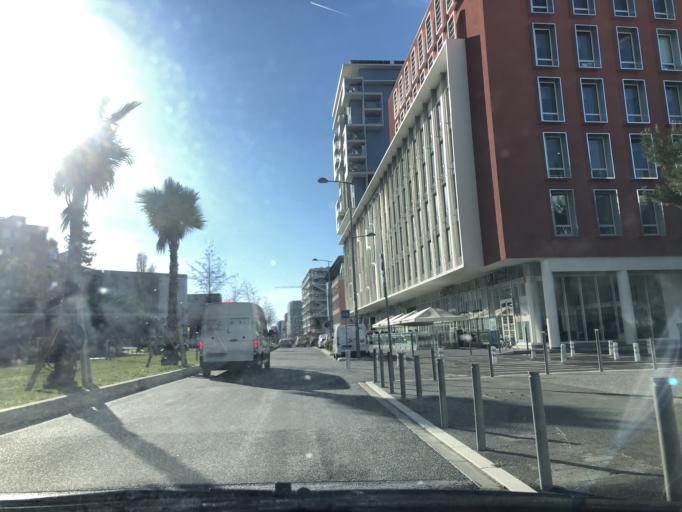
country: FR
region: Provence-Alpes-Cote d'Azur
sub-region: Departement des Alpes-Maritimes
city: Saint-Laurent-du-Var
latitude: 43.6851
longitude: 7.2023
